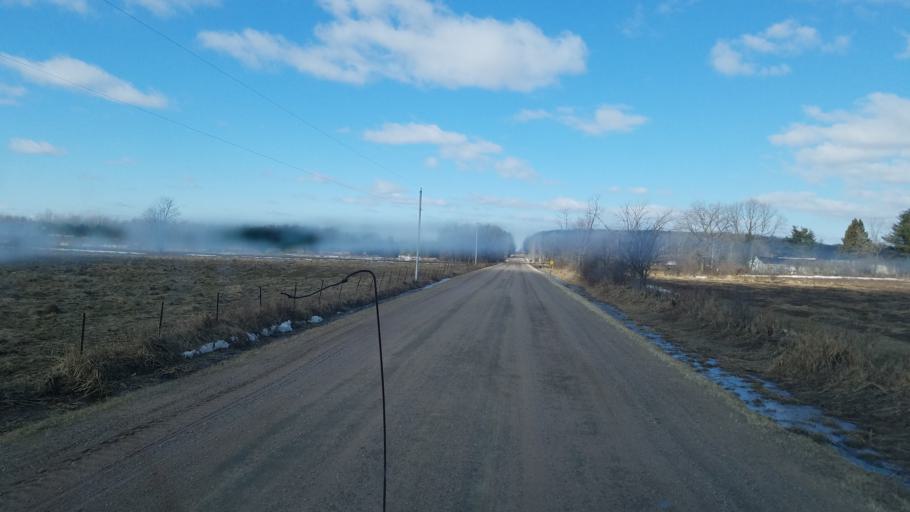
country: US
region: Wisconsin
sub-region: Clark County
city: Loyal
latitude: 44.6256
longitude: -90.4200
